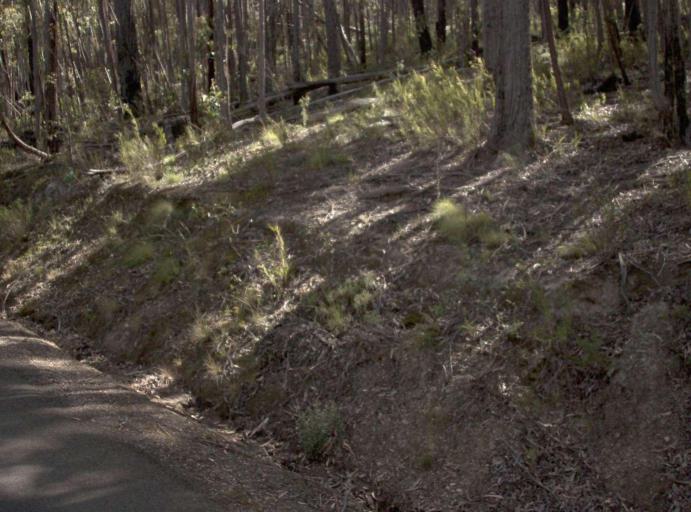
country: AU
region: Victoria
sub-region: East Gippsland
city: Lakes Entrance
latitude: -37.4414
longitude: 148.1315
